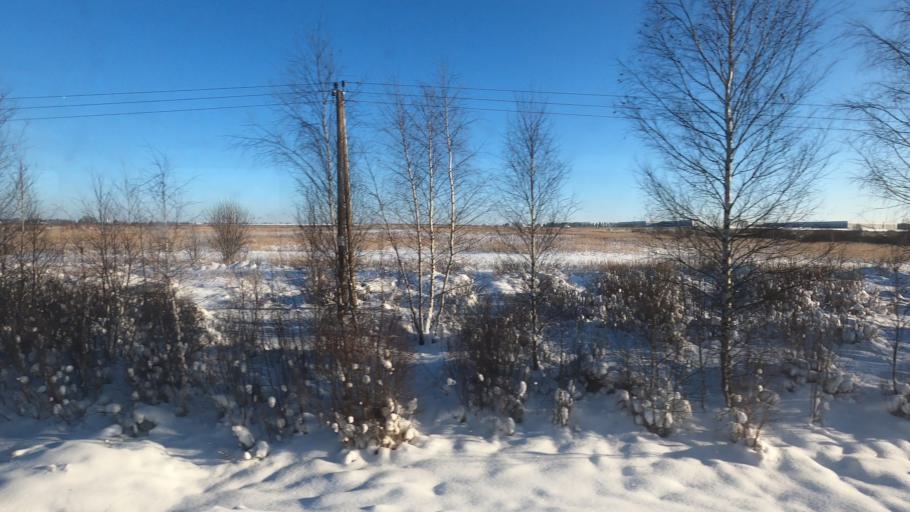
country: RU
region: Moskovskaya
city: Orud'yevo
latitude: 56.4263
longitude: 37.4984
